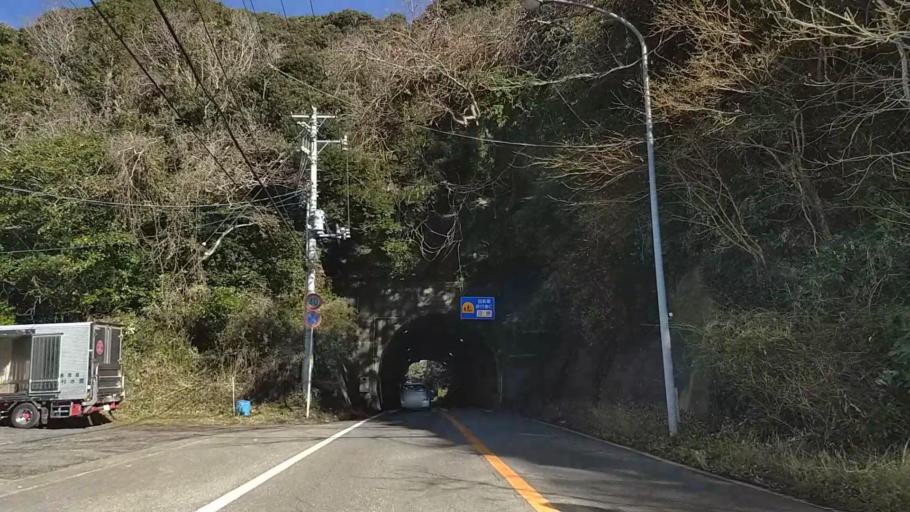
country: JP
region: Chiba
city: Katsuura
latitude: 35.1566
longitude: 140.3239
